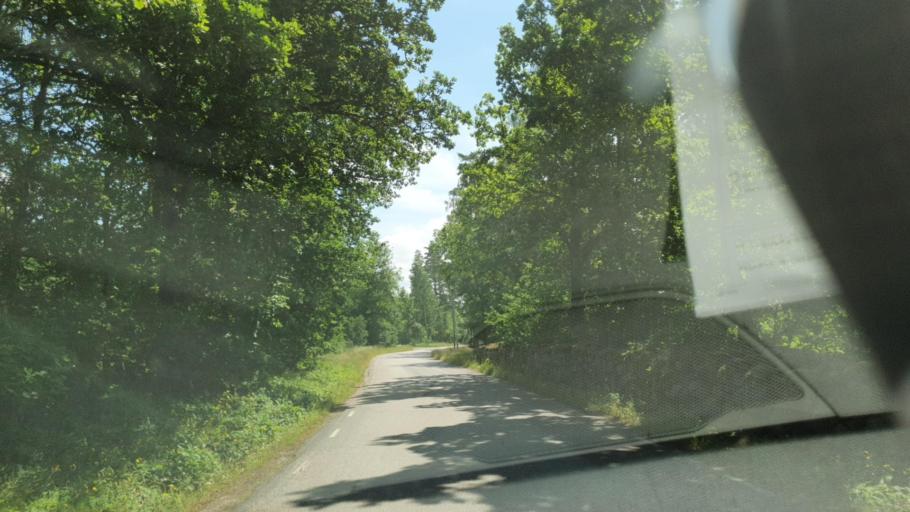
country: SE
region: Kronoberg
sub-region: Lessebo Kommun
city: Hovmantorp
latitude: 56.7445
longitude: 15.1778
